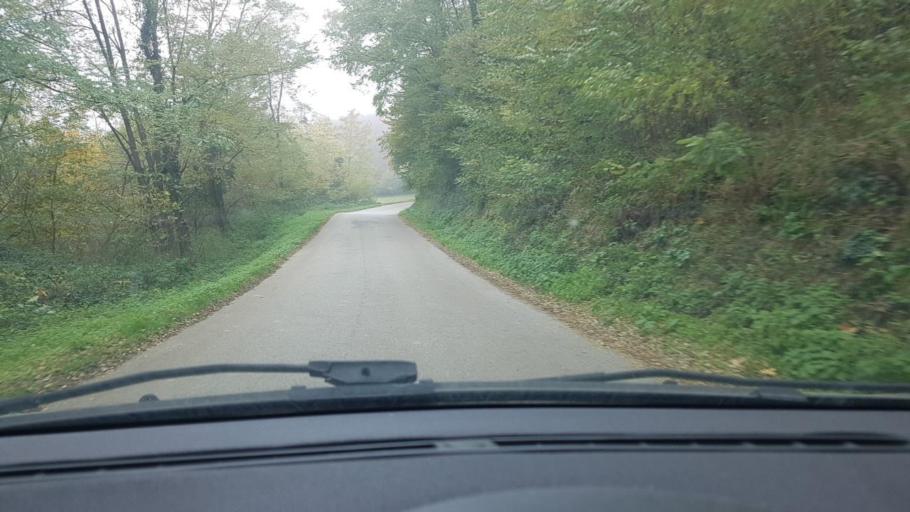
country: HR
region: Krapinsko-Zagorska
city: Mihovljan
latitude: 46.1413
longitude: 15.9773
